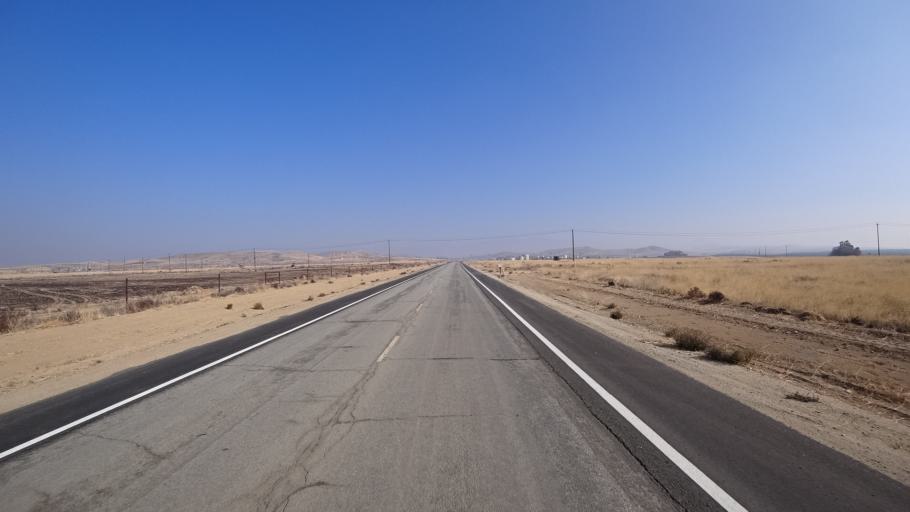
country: US
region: California
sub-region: Kern County
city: Lamont
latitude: 35.3701
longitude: -118.8512
